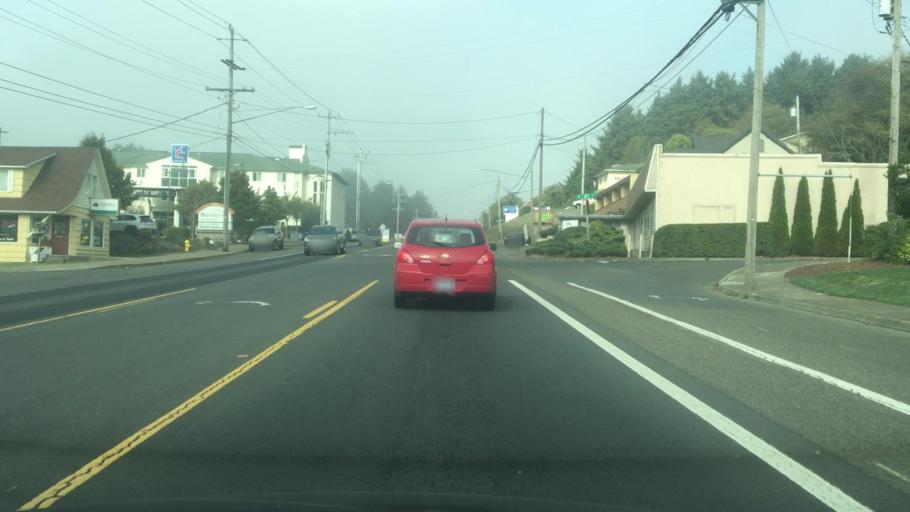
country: US
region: Oregon
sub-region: Lincoln County
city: Lincoln City
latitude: 44.9900
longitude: -124.0059
